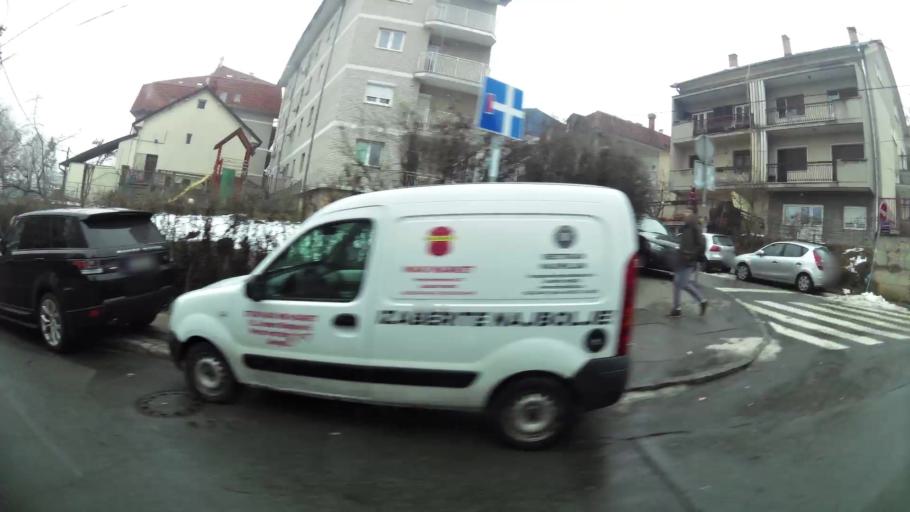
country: RS
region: Central Serbia
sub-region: Belgrade
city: Cukarica
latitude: 44.7741
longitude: 20.4166
